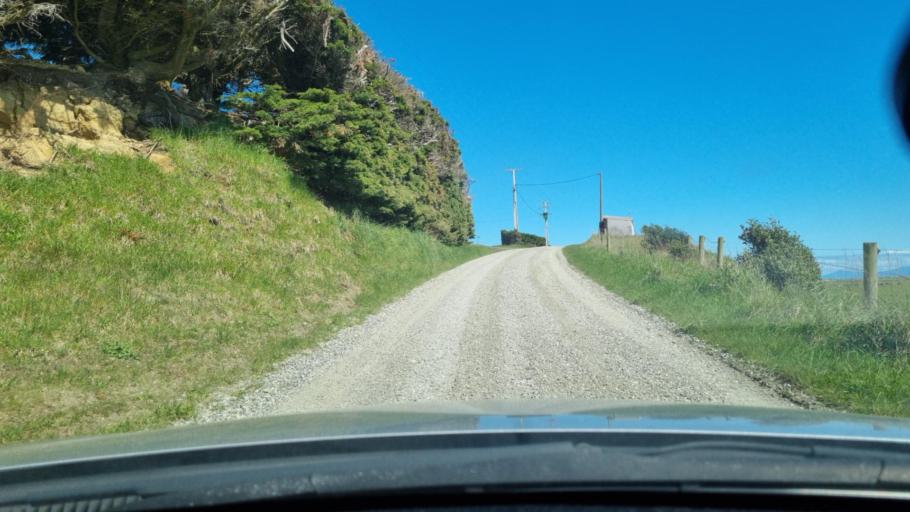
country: NZ
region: Southland
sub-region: Invercargill City
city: Invercargill
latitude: -46.3933
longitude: 168.2582
